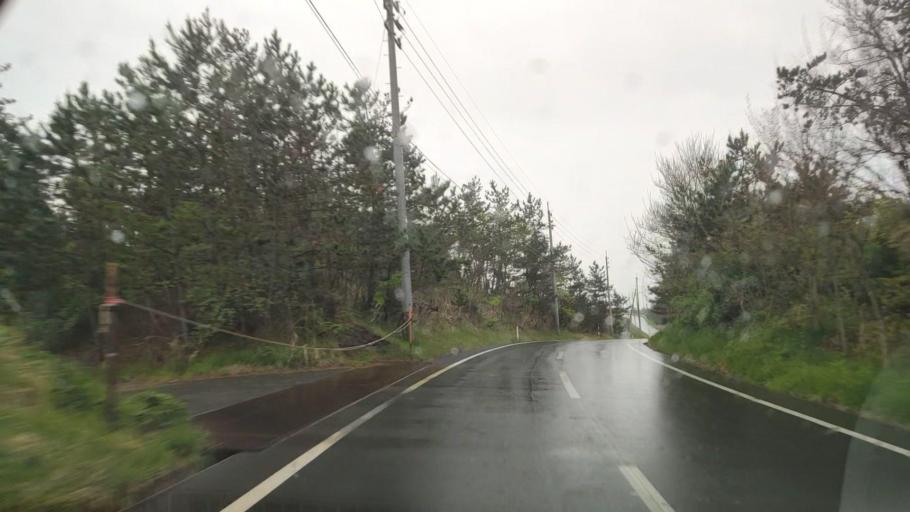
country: JP
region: Akita
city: Noshiromachi
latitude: 40.0793
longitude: 139.9540
